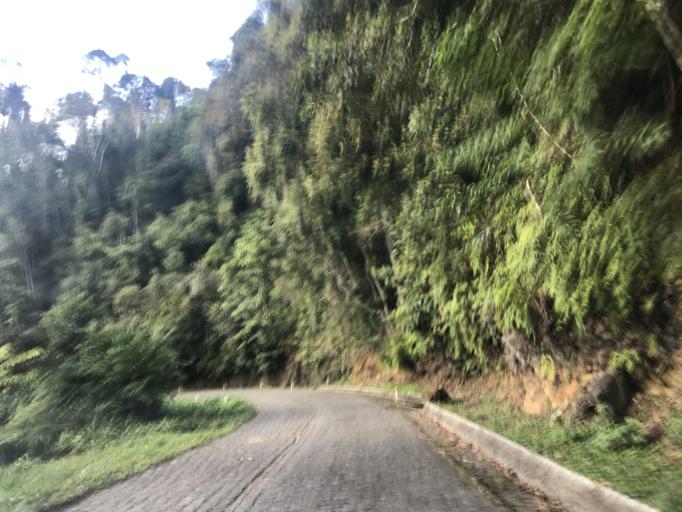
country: BR
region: Bahia
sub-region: Gandu
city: Gandu
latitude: -13.9082
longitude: -39.4650
